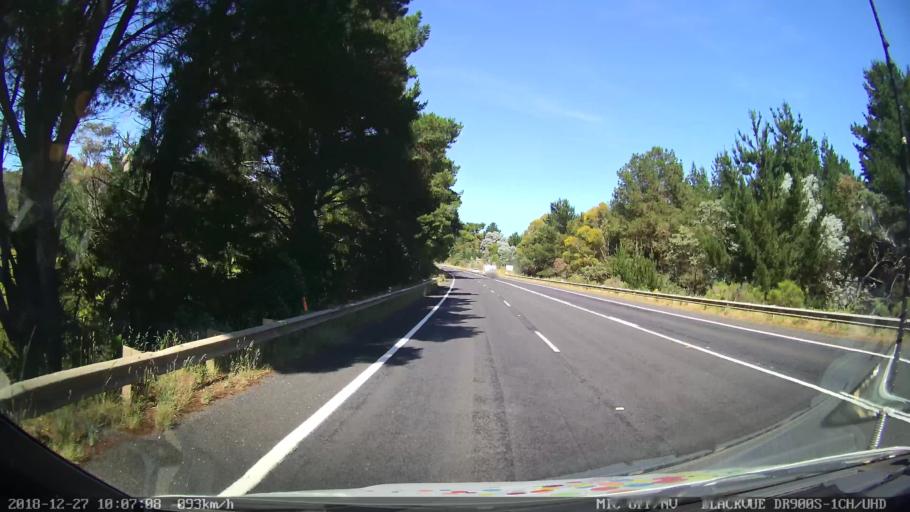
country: AU
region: New South Wales
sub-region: Lithgow
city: Portland
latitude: -33.4383
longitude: 149.8440
